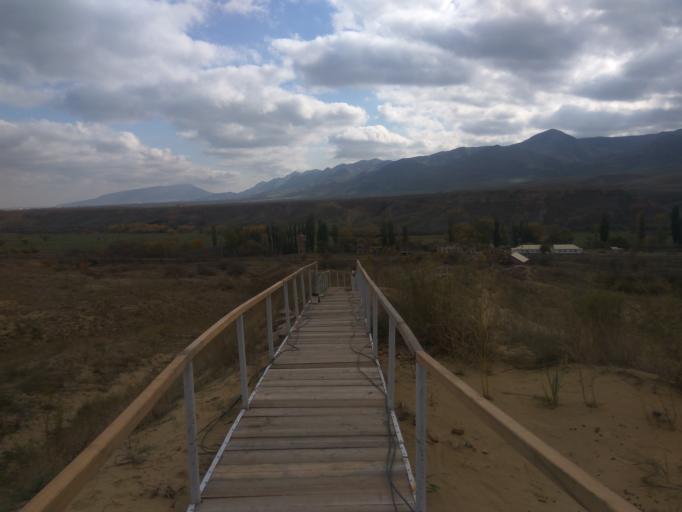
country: RU
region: Dagestan
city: Korkmaskala
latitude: 43.0058
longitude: 47.2351
